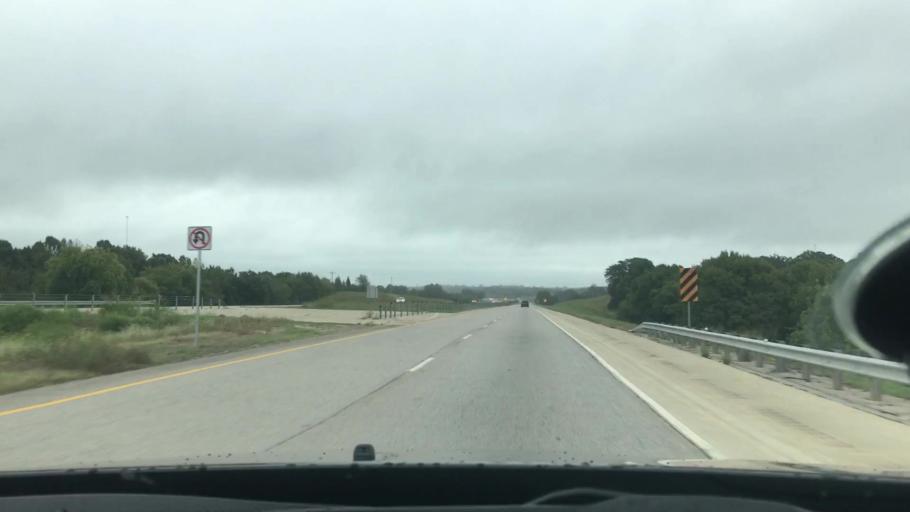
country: US
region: Oklahoma
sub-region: Okfuskee County
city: Boley
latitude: 35.3870
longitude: -96.4417
